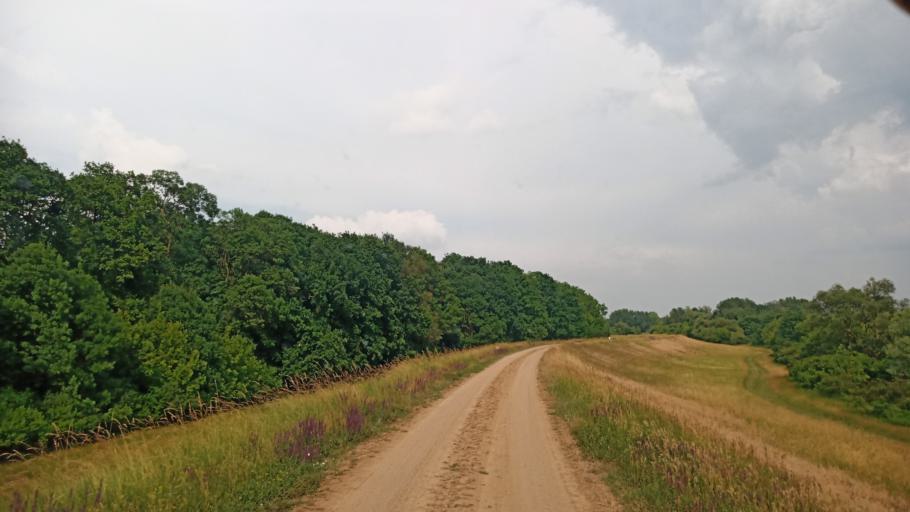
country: HU
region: Bekes
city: Doboz
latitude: 46.7074
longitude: 21.2963
